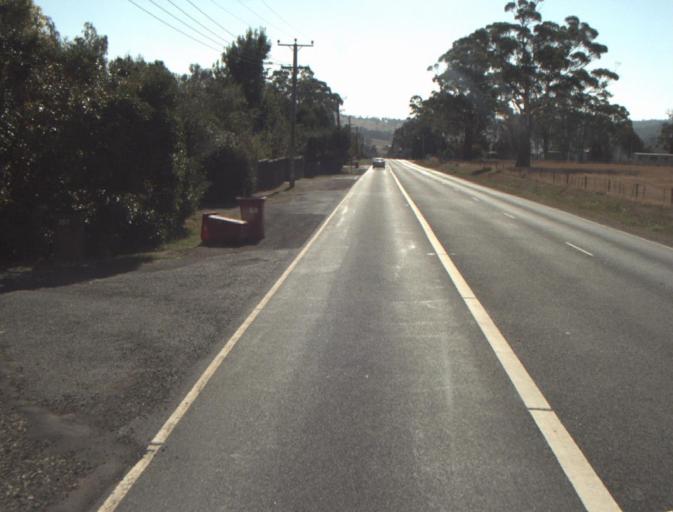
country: AU
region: Tasmania
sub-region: Launceston
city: Mayfield
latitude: -41.3389
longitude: 147.0839
